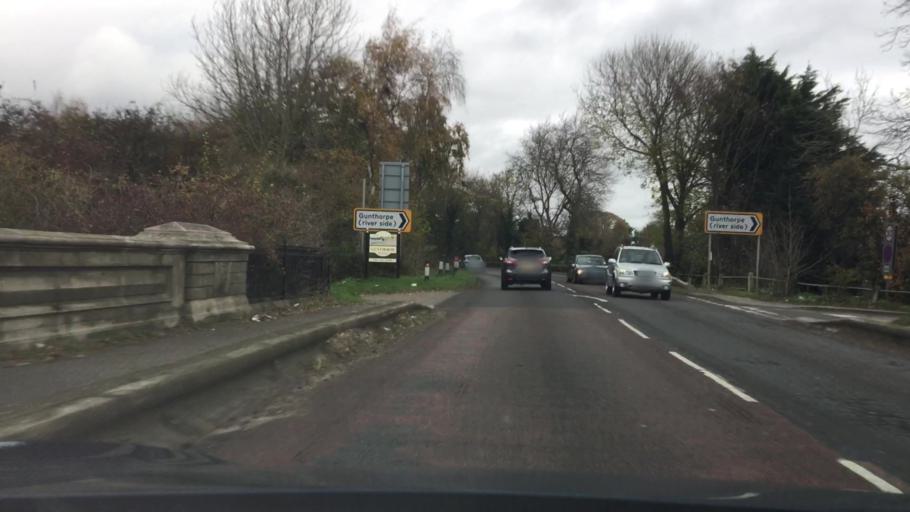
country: GB
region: England
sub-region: Nottinghamshire
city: East Bridgford
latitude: 52.9868
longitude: -0.9873
